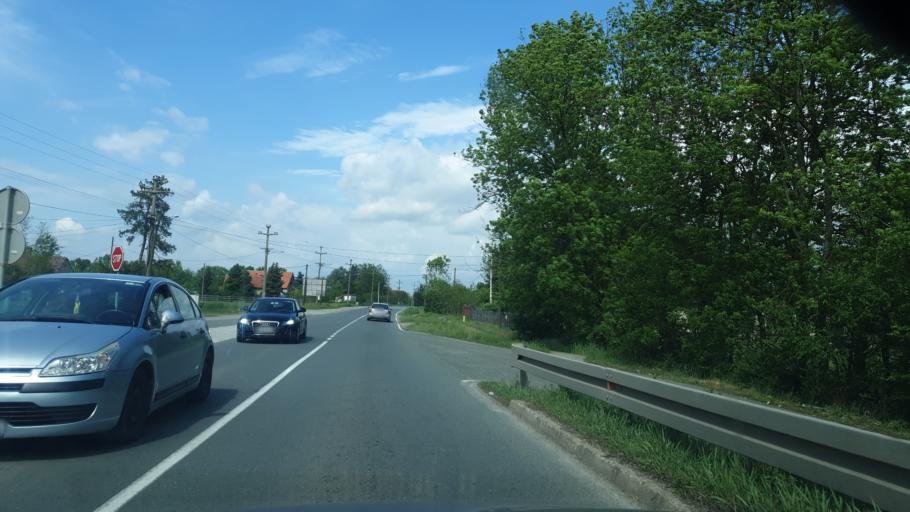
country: RS
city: Zvecka
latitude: 44.6108
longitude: 20.1578
